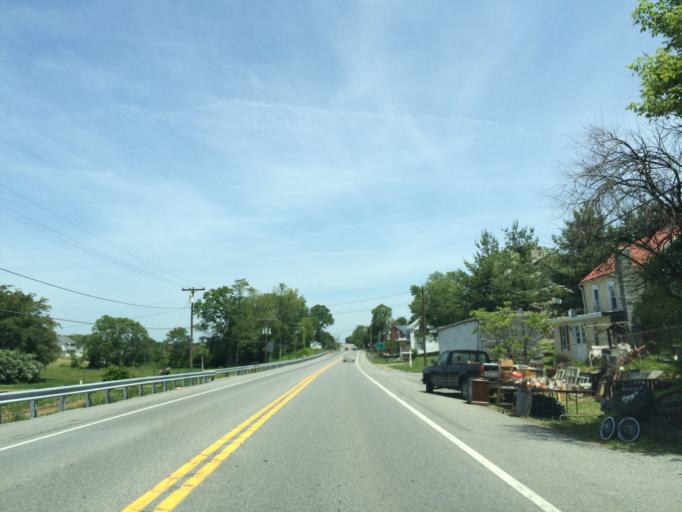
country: US
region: Maryland
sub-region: Washington County
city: Saint James
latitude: 39.5348
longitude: -77.7403
